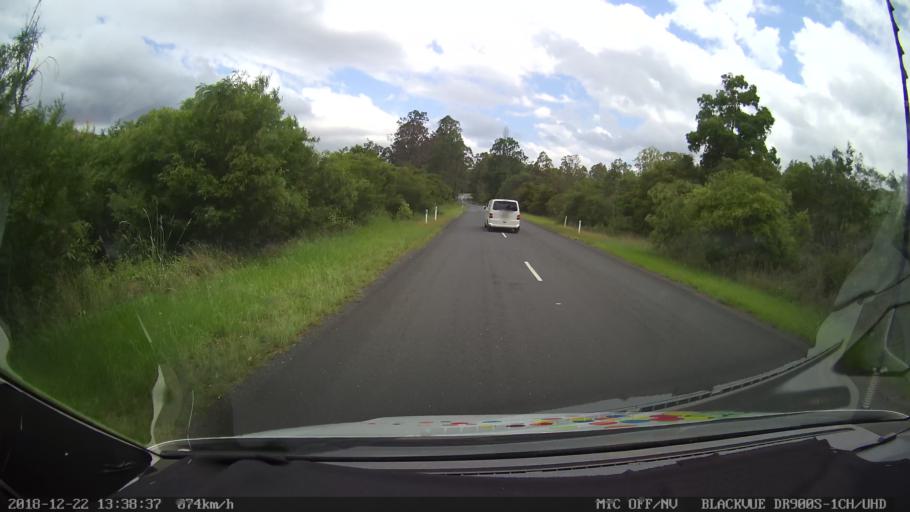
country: AU
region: New South Wales
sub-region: Clarence Valley
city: Coutts Crossing
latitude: -29.9019
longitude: 152.7862
